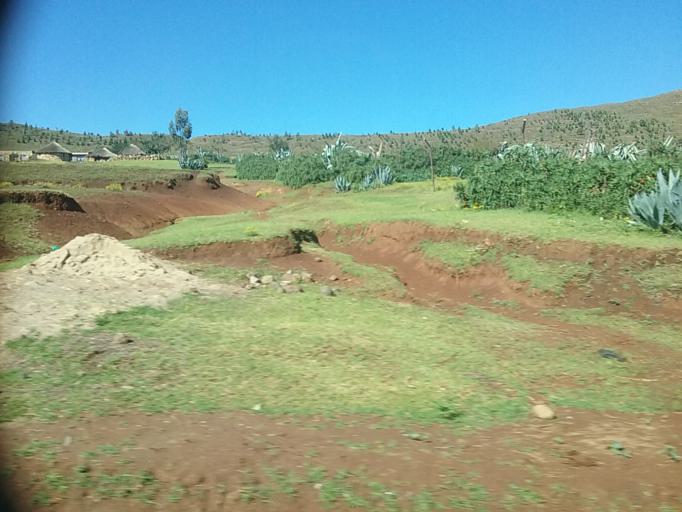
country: LS
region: Berea
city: Teyateyaneng
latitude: -29.2304
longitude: 27.8817
